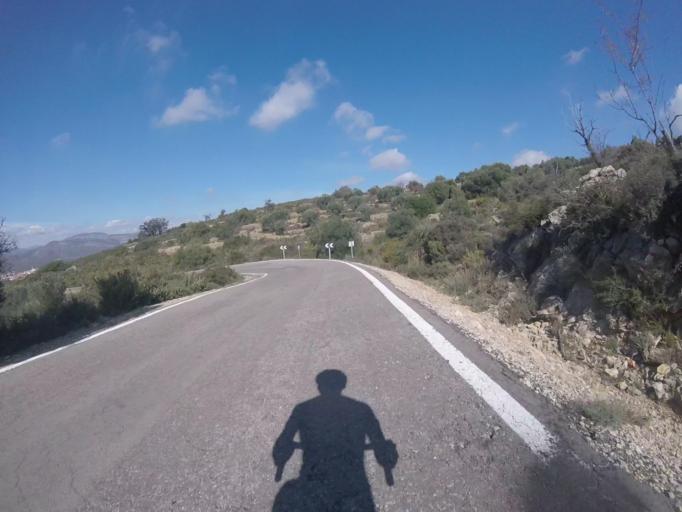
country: ES
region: Valencia
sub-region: Provincia de Castello
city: Albocasser
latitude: 40.3531
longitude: 0.0459
